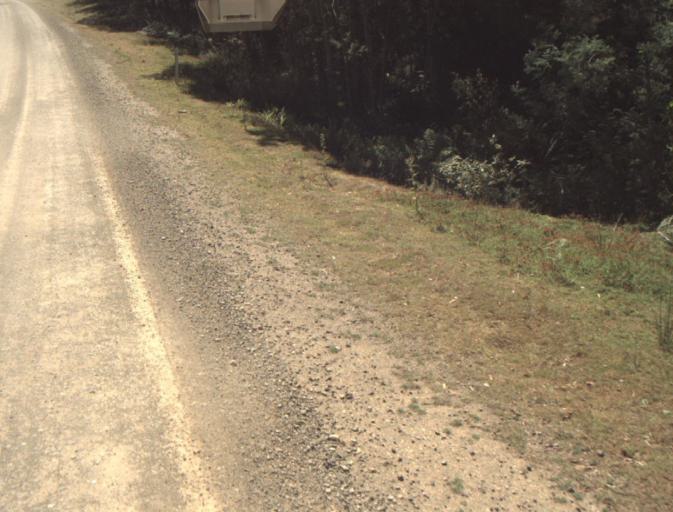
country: AU
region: Tasmania
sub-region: Dorset
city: Scottsdale
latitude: -41.3770
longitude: 147.4778
